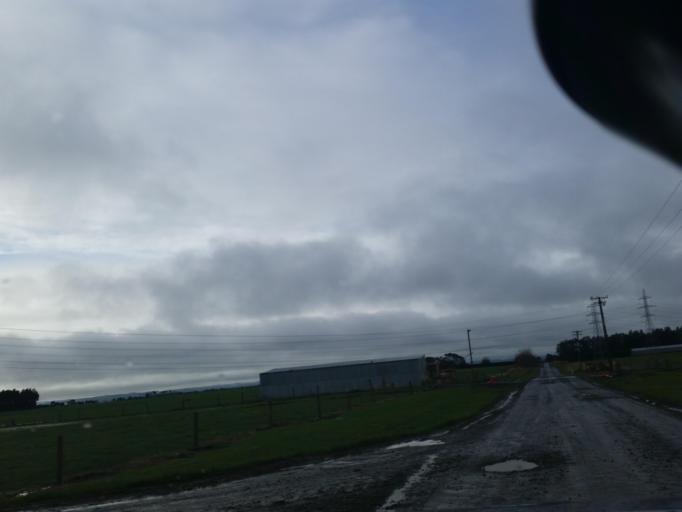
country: NZ
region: Southland
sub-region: Southland District
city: Winton
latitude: -46.2055
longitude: 168.1954
